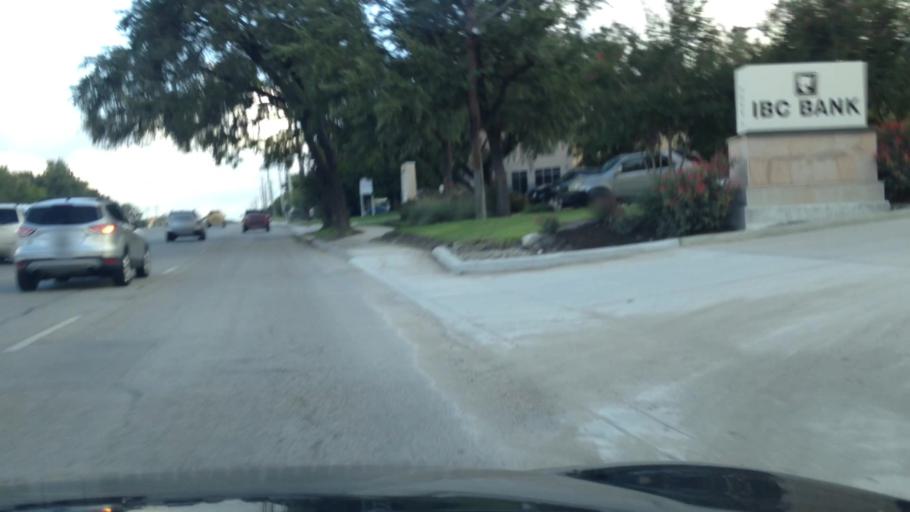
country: US
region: Texas
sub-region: Bexar County
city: Balcones Heights
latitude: 29.5226
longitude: -98.5739
